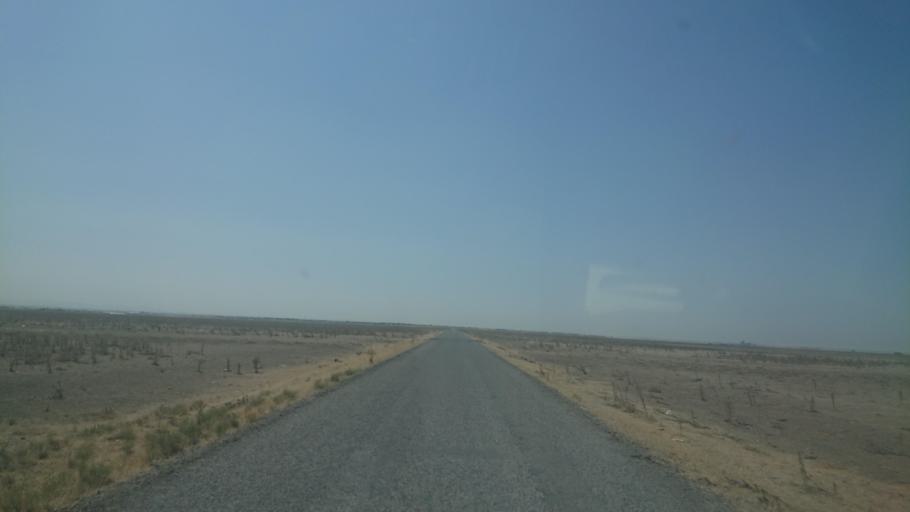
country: TR
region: Aksaray
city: Yesilova
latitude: 38.3226
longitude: 33.7445
